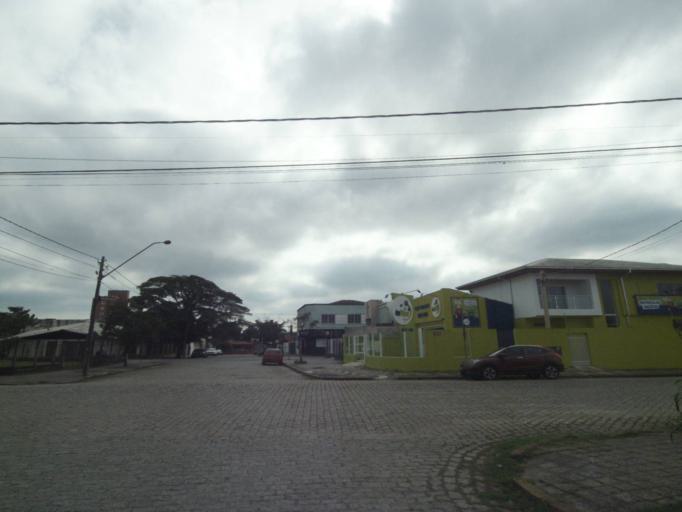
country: BR
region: Parana
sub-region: Paranagua
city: Paranagua
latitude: -25.5238
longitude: -48.5130
